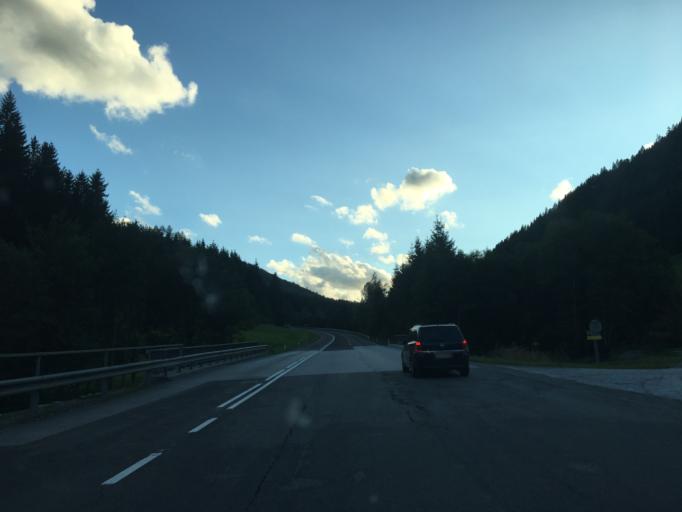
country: AT
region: Styria
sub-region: Politischer Bezirk Murtal
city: Hohentauern
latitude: 47.4380
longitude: 14.5005
